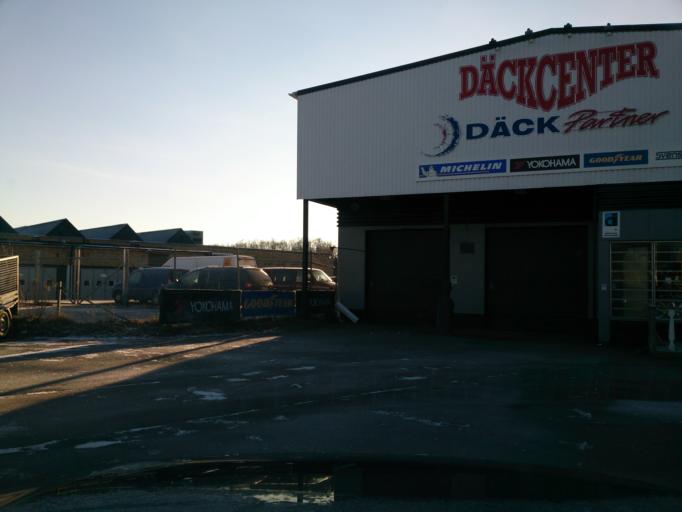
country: SE
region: OEstergoetland
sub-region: Norrkopings Kommun
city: Norrkoping
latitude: 58.6001
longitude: 16.1469
